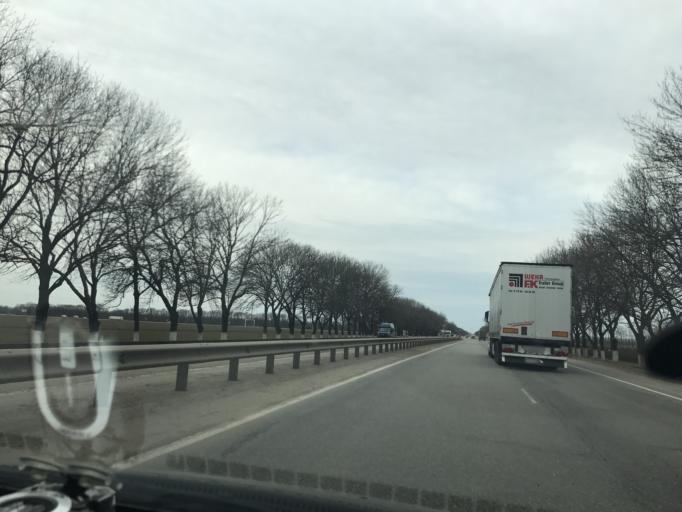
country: RU
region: Krasnodarskiy
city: Zavetnyy
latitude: 44.9467
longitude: 41.0922
